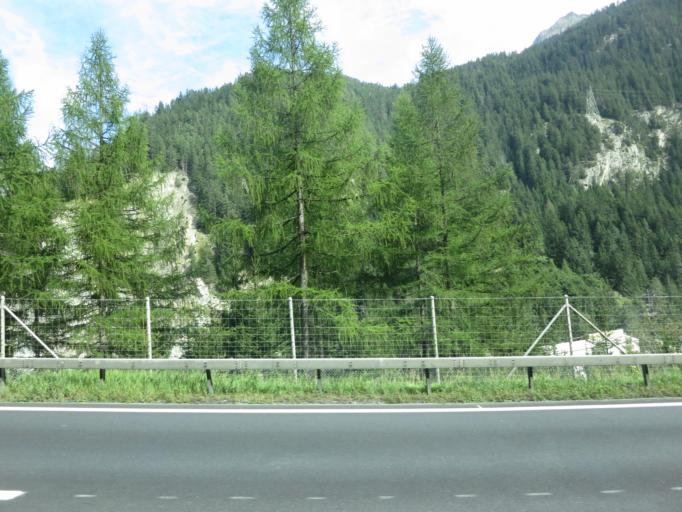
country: CH
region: Grisons
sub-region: Hinterrhein District
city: Thusis
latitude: 46.5789
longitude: 9.4252
